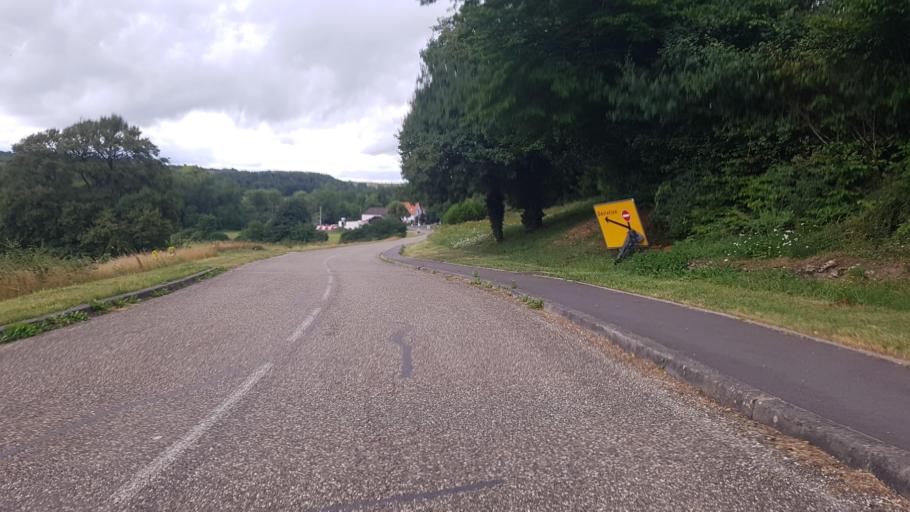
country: FR
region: Lorraine
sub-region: Departement de la Moselle
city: Lorquin
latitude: 48.7020
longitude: 6.9940
